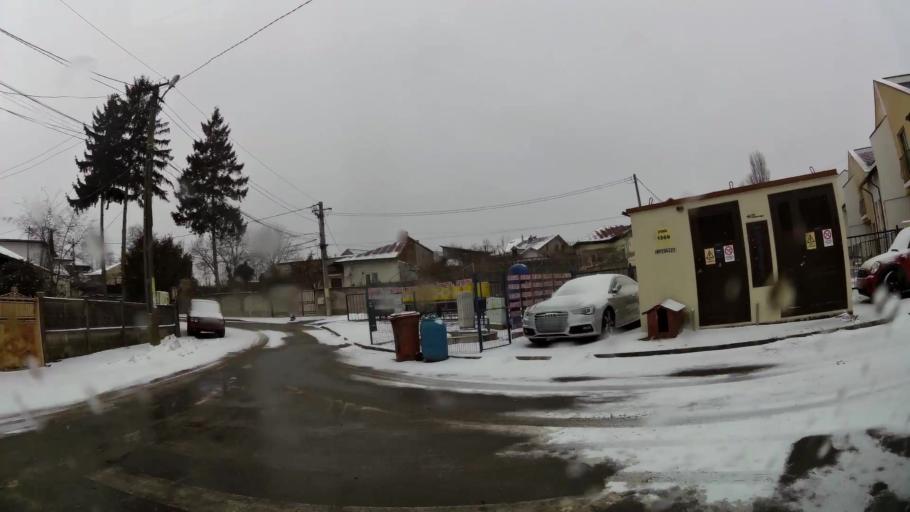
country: RO
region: Dambovita
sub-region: Municipiul Targoviste
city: Targoviste
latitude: 44.9236
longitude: 25.4763
